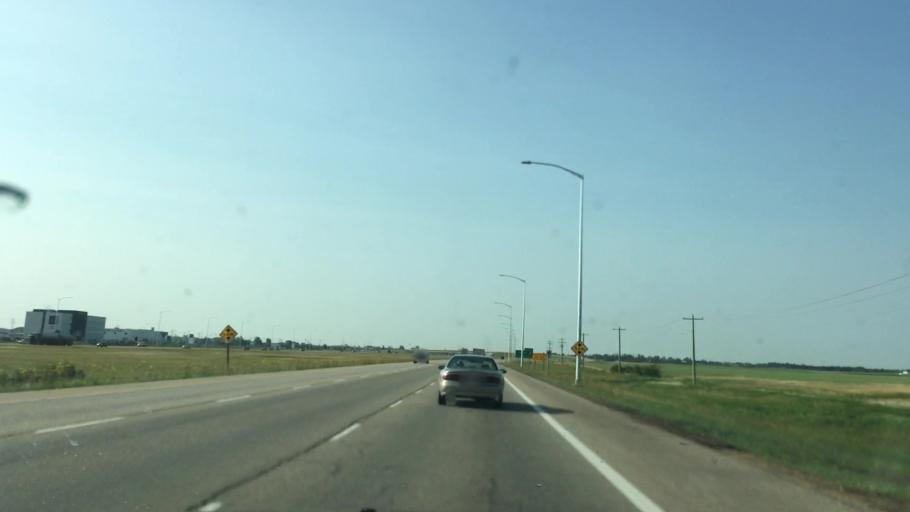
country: CA
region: Alberta
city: Leduc
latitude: 53.2959
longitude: -113.5499
